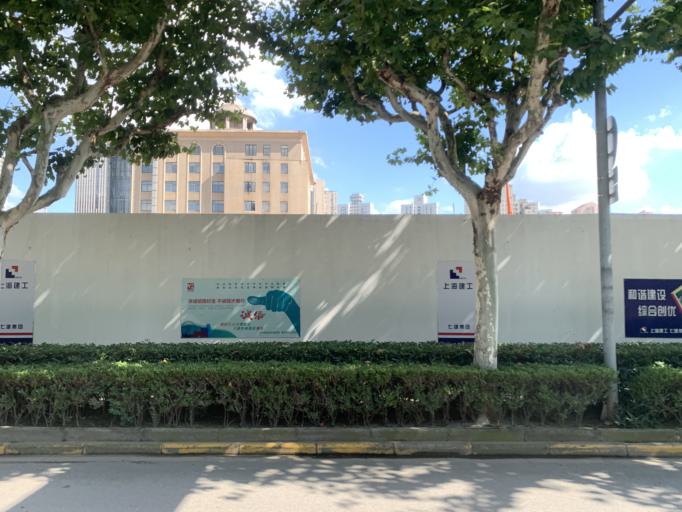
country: CN
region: Shanghai Shi
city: Pudong
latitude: 31.2381
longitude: 121.5267
